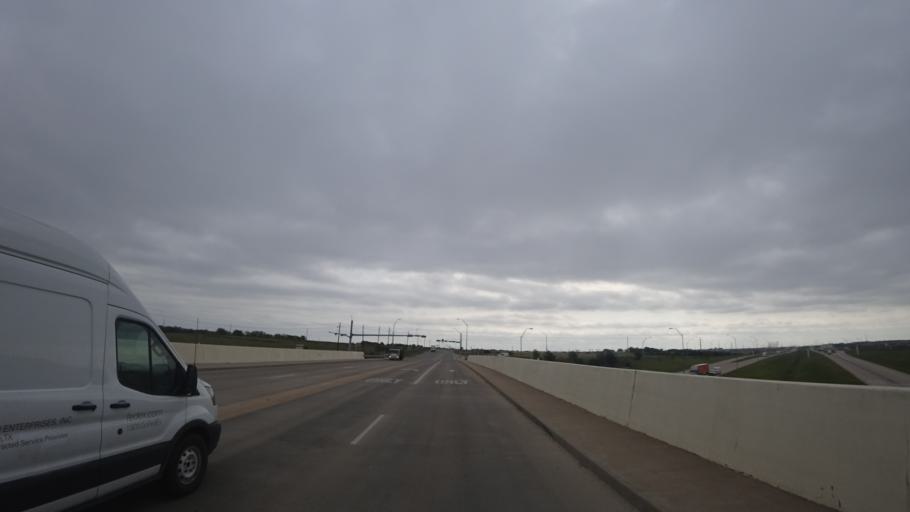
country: US
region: Texas
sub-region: Travis County
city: Pflugerville
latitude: 30.4236
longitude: -97.5881
